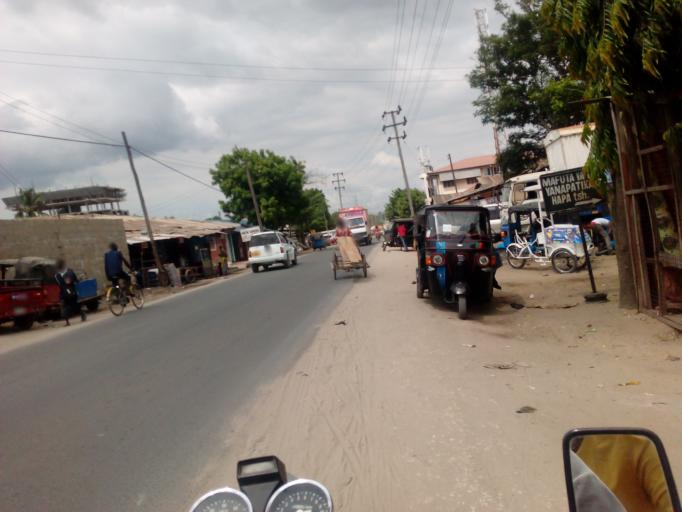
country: TZ
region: Dar es Salaam
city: Dar es Salaam
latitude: -6.8559
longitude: 39.2544
